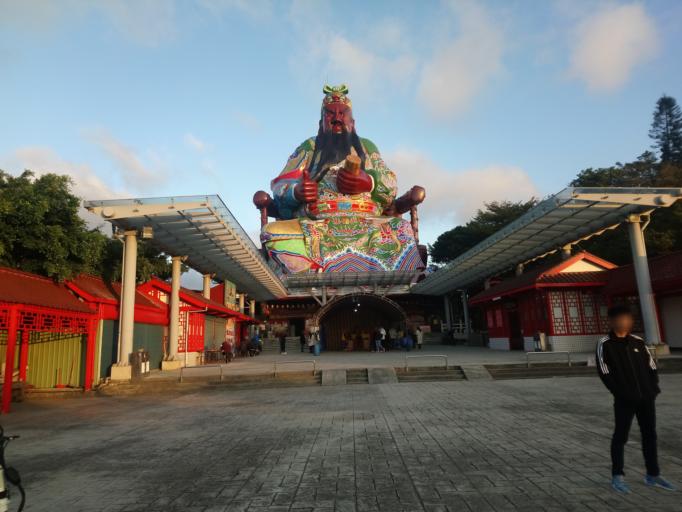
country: TW
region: Taiwan
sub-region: Hsinchu
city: Hsinchu
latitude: 24.7806
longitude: 120.9782
